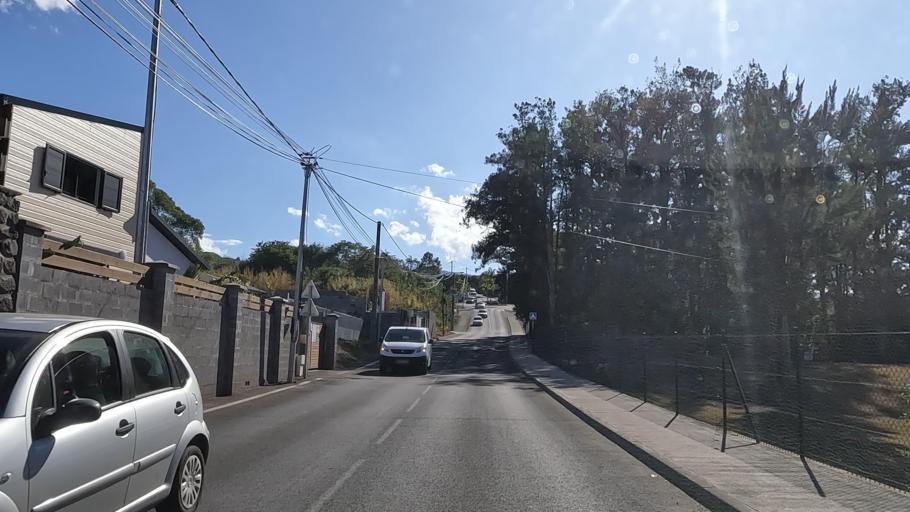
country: RE
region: Reunion
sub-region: Reunion
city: Le Tampon
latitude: -21.2590
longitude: 55.5112
